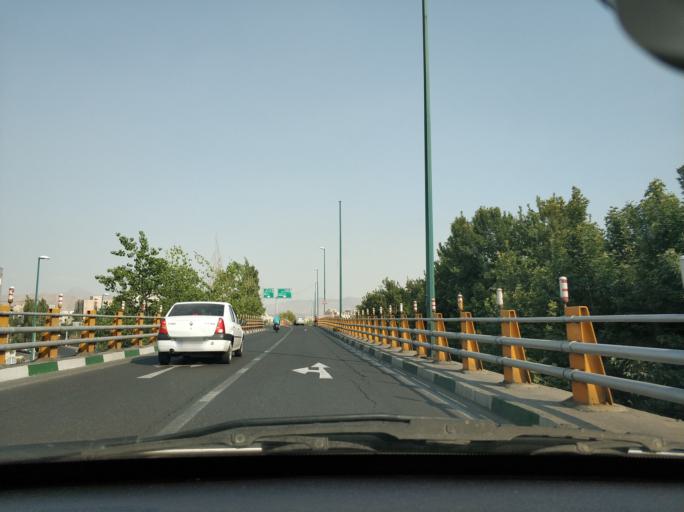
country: IR
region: Tehran
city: Tehran
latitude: 35.7228
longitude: 51.4733
